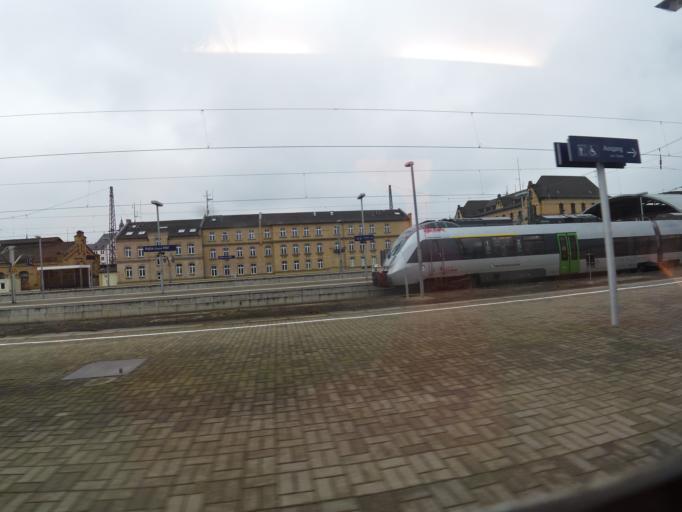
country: DE
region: Saxony-Anhalt
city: Halle (Saale)
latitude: 51.4768
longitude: 11.9891
